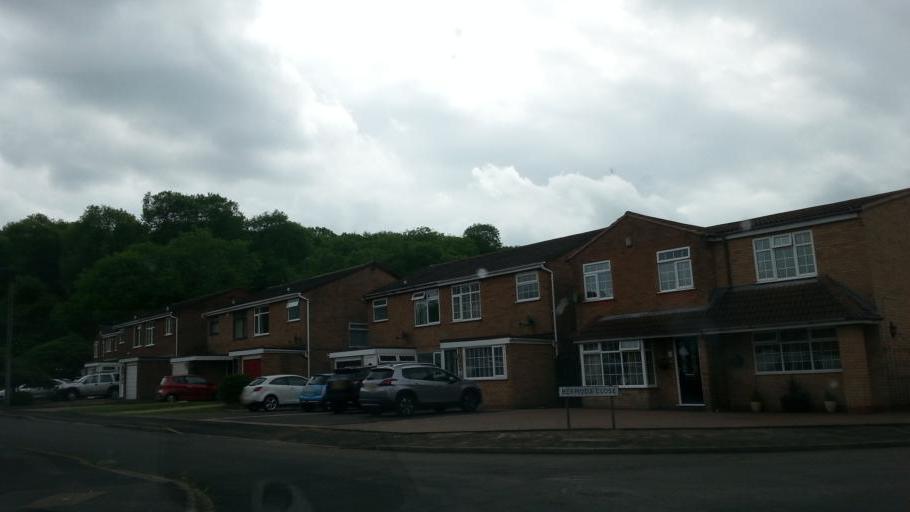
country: GB
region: England
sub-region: Sandwell
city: Tipton
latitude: 52.5324
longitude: -2.0931
